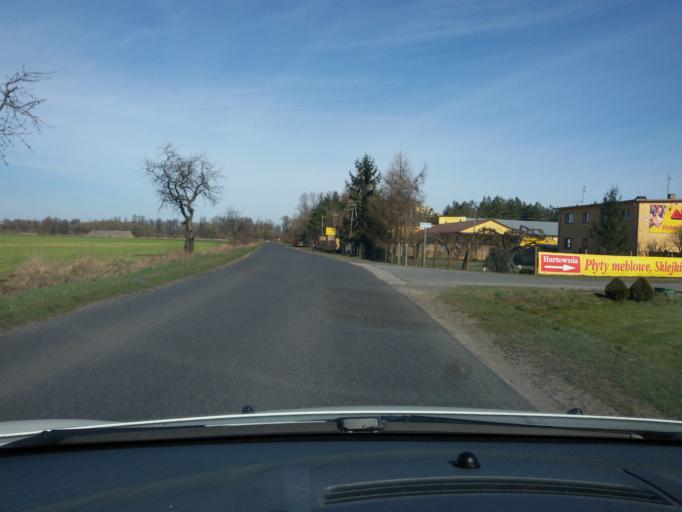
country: PL
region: Greater Poland Voivodeship
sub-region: Powiat gostynski
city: Krobia
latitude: 51.7589
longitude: 16.9088
